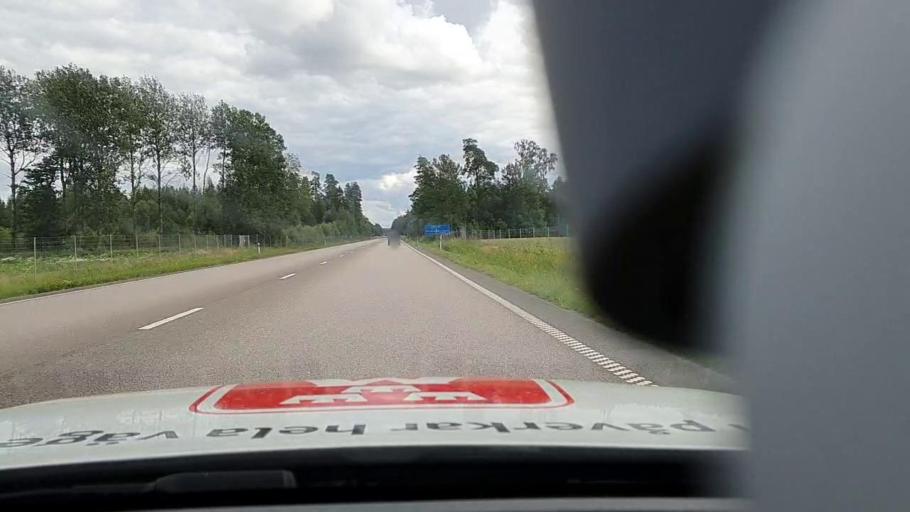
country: SE
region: Vaestra Goetaland
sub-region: Lidkopings Kommun
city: Vinninga
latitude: 58.4667
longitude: 13.2175
